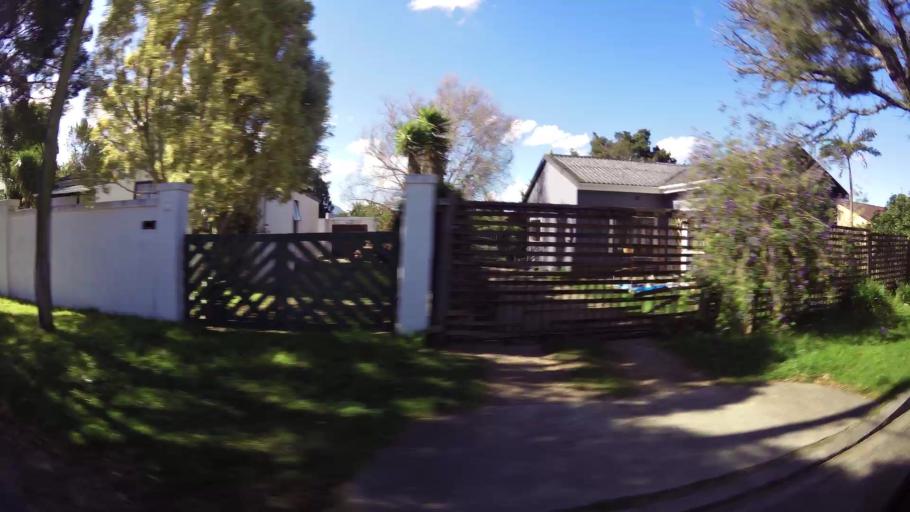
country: ZA
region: Western Cape
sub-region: Eden District Municipality
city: George
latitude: -33.9434
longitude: 22.4721
